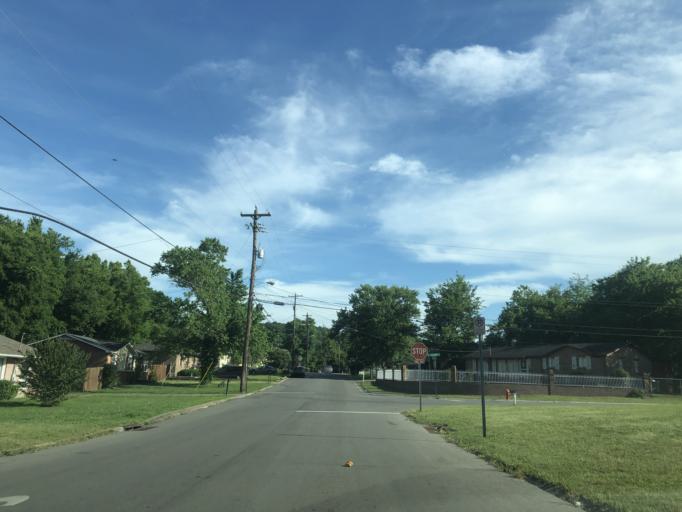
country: US
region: Tennessee
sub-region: Davidson County
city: Nashville
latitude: 36.2121
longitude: -86.8339
